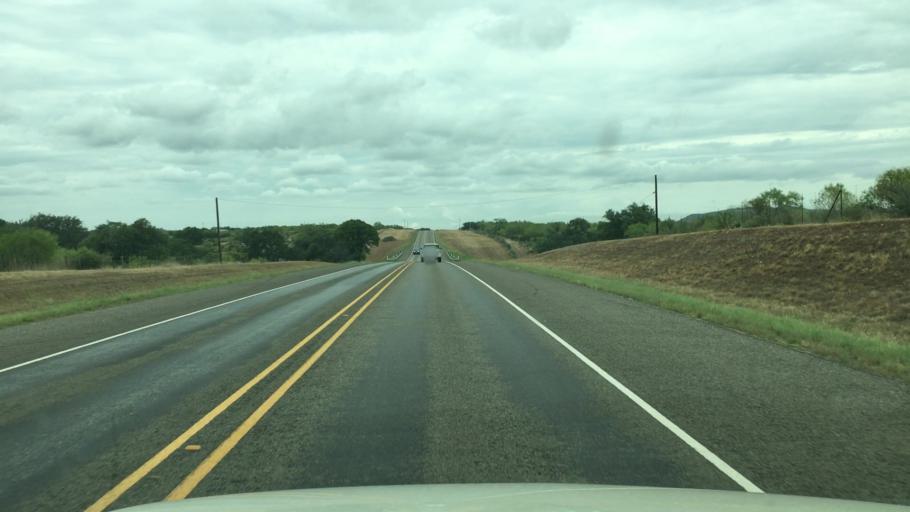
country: US
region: Texas
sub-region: Llano County
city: Kingsland
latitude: 30.5726
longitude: -98.4891
